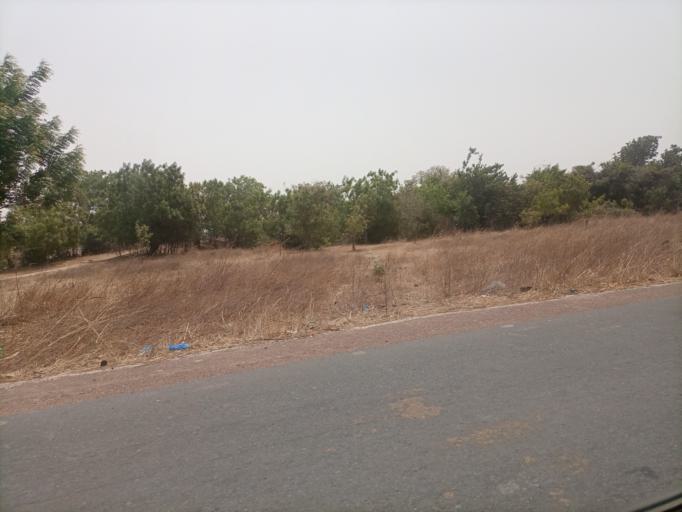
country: SN
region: Fatick
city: Sokone
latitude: 13.7304
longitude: -16.4217
